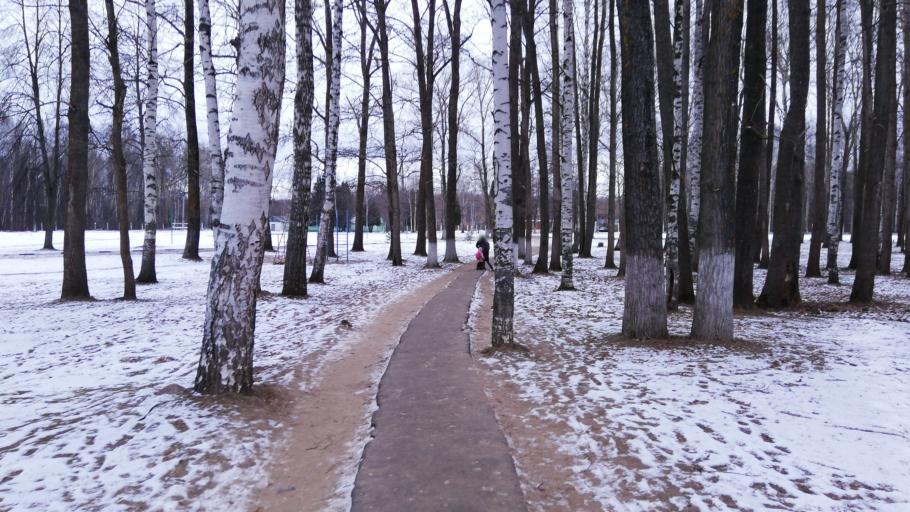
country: RU
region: Jaroslavl
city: Yaroslavl
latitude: 57.7229
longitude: 39.8148
